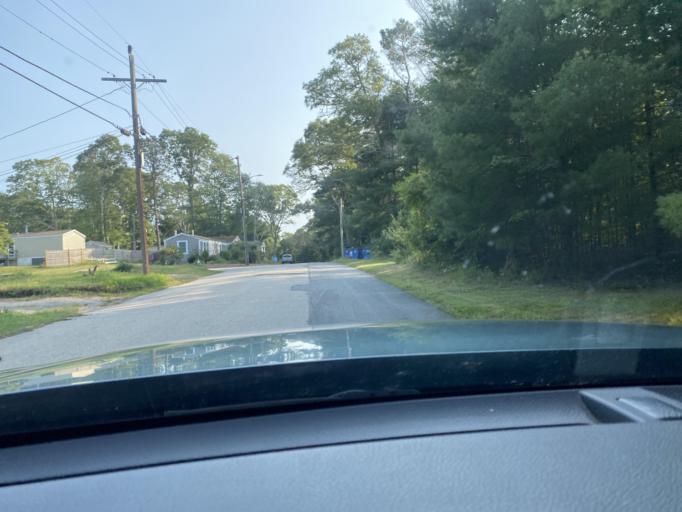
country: US
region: Massachusetts
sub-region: Barnstable County
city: Mashpee
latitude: 41.6144
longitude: -70.5145
